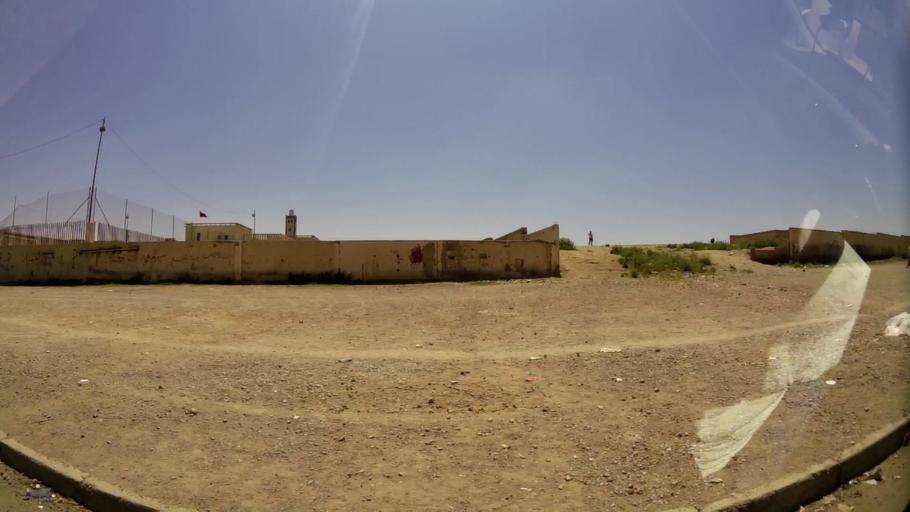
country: MA
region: Oriental
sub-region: Oujda-Angad
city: Oujda
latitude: 34.6927
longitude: -1.9440
